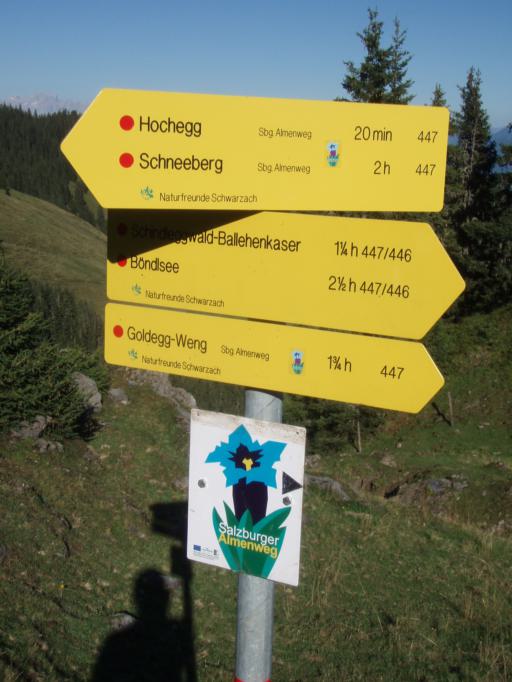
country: AT
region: Salzburg
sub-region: Politischer Bezirk Sankt Johann im Pongau
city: Goldegg
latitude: 47.3473
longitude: 13.0675
